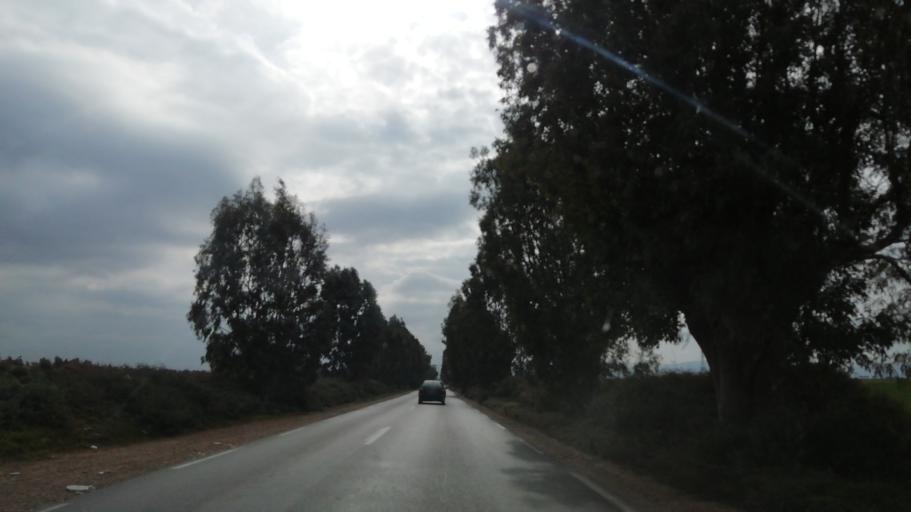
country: DZ
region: Oran
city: Sidi ech Chahmi
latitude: 35.5803
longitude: -0.4523
